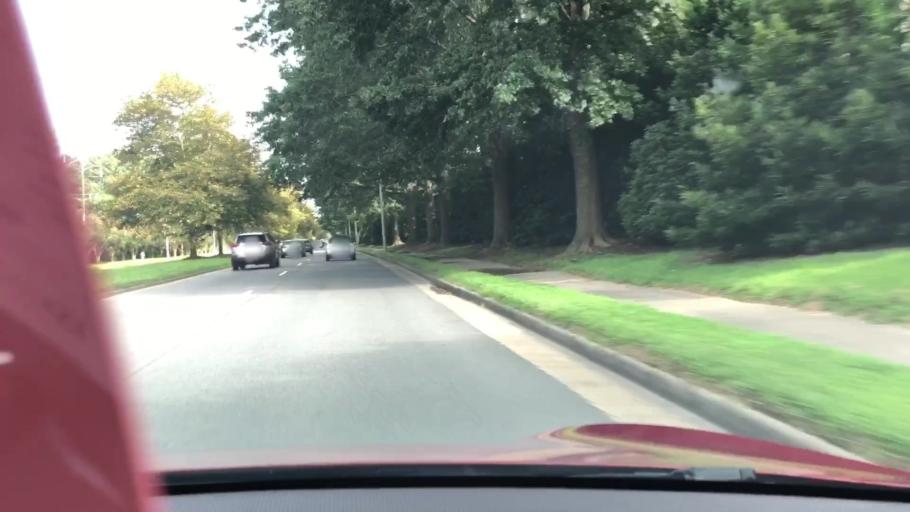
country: US
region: Virginia
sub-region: City of Virginia Beach
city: Virginia Beach
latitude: 36.8937
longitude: -76.0582
